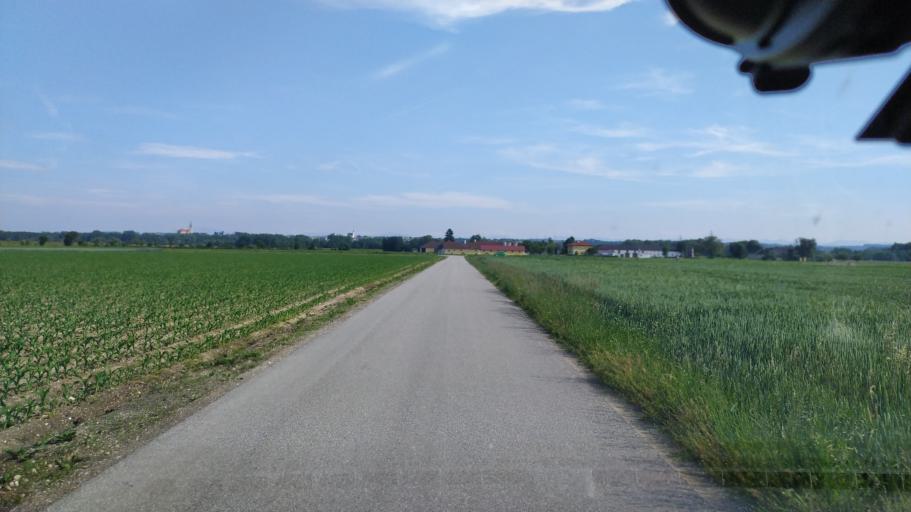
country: AT
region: Lower Austria
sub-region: Politischer Bezirk Amstetten
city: Strengberg
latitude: 48.1869
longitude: 14.6862
